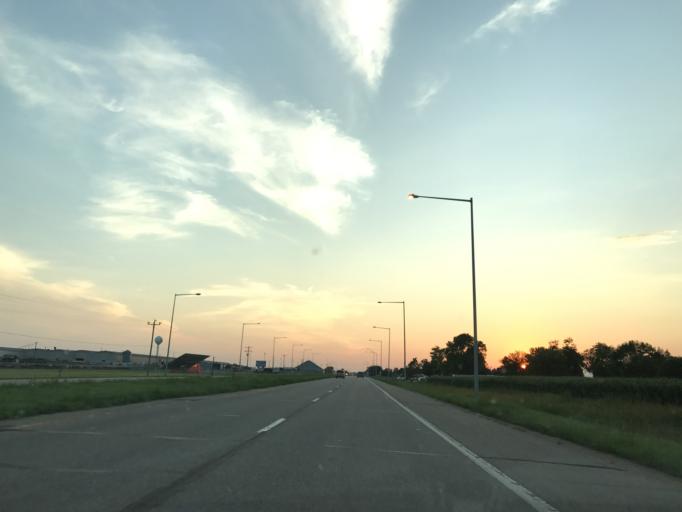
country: US
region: Nebraska
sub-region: Platte County
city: Columbus
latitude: 41.4386
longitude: -97.2720
